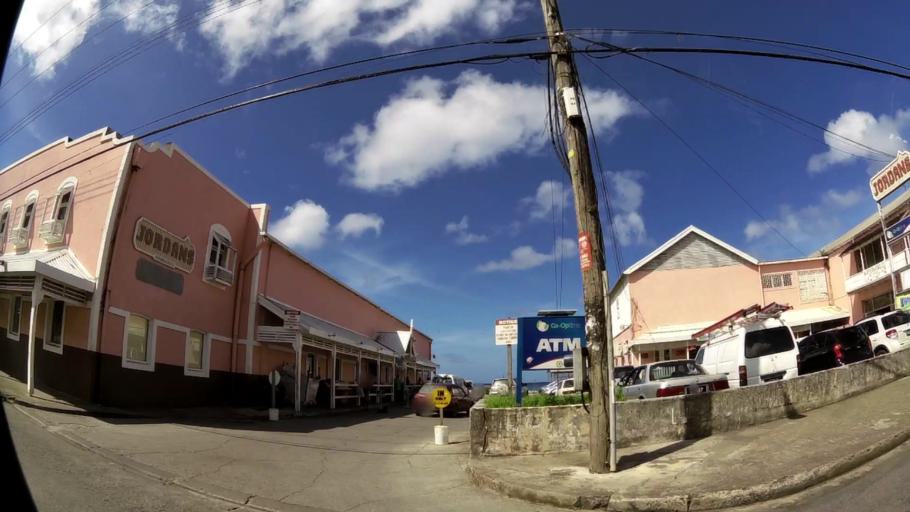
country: BB
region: Saint Peter
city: Speightstown
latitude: 13.2478
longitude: -59.6436
